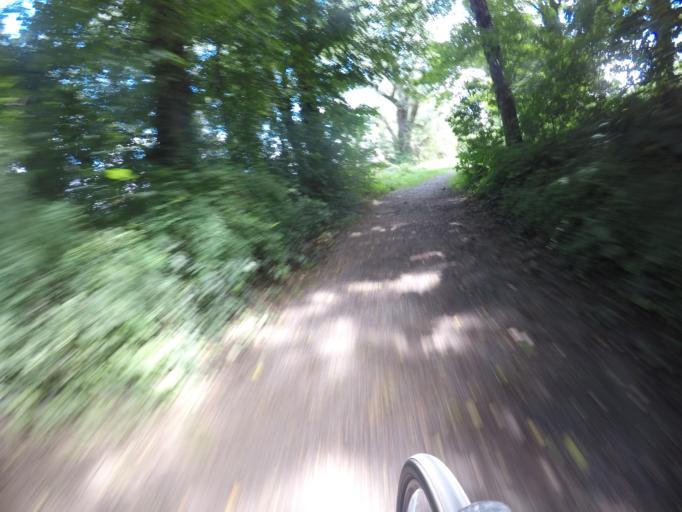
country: DE
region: Baden-Wuerttemberg
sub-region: Tuebingen Region
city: Rottenburg
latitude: 48.4743
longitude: 8.9413
